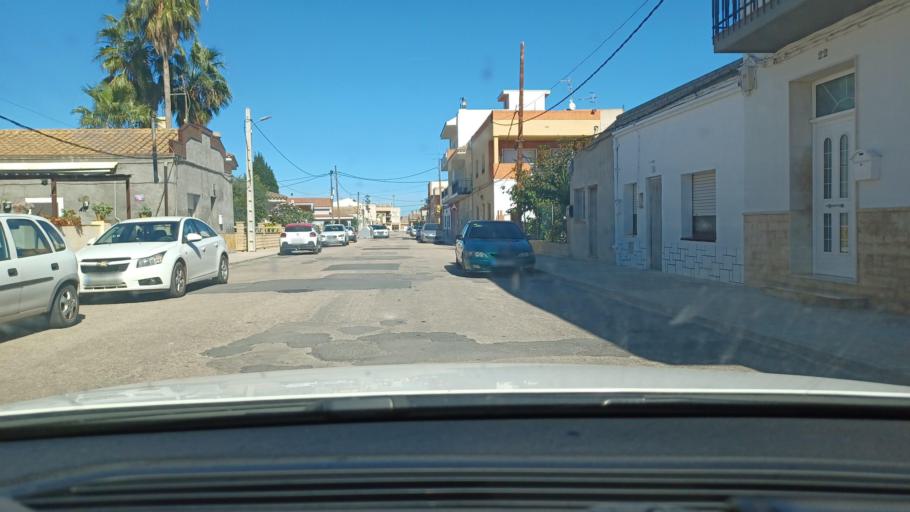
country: ES
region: Catalonia
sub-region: Provincia de Tarragona
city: Deltebre
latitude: 40.7178
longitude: 0.7400
